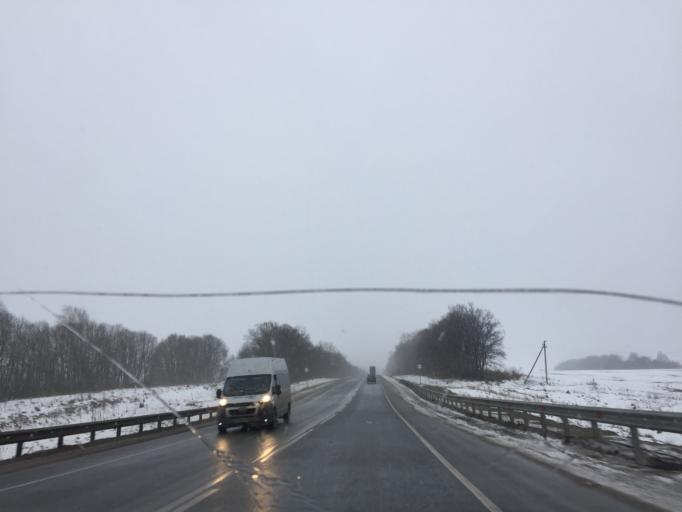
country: RU
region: Tula
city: Plavsk
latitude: 53.8069
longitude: 37.3862
